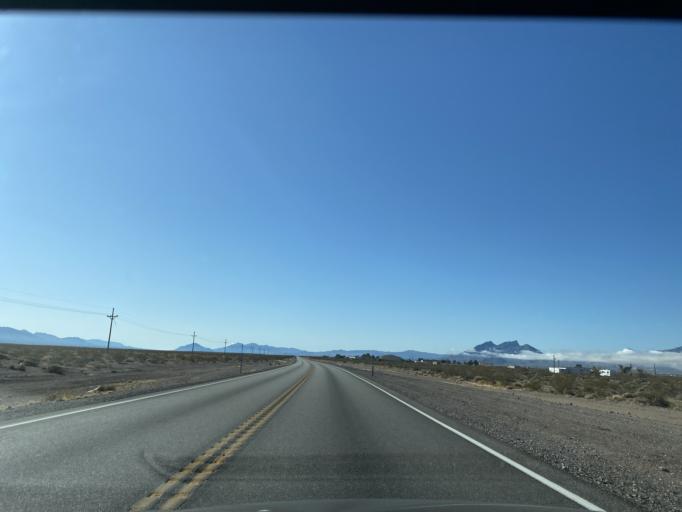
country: US
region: Nevada
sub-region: Nye County
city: Beatty
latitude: 36.5044
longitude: -116.4212
